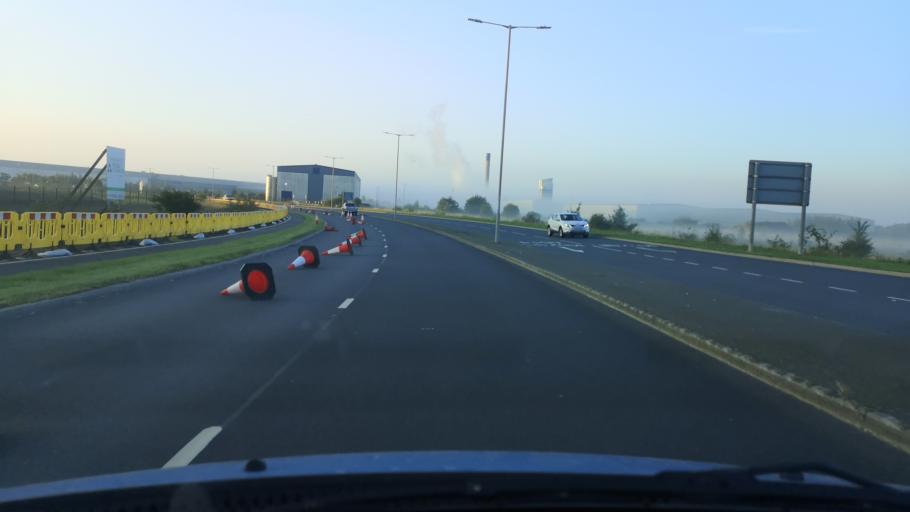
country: GB
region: England
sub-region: East Riding of Yorkshire
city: Airmyn
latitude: 53.7034
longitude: -0.9089
